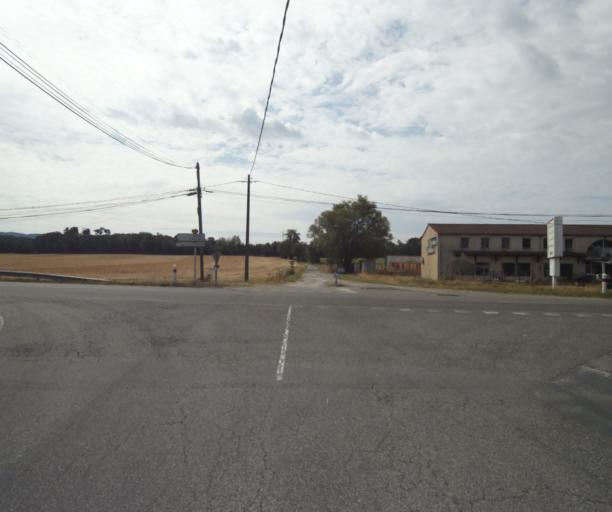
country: FR
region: Midi-Pyrenees
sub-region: Departement de la Haute-Garonne
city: Revel
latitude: 43.4478
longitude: 1.9621
